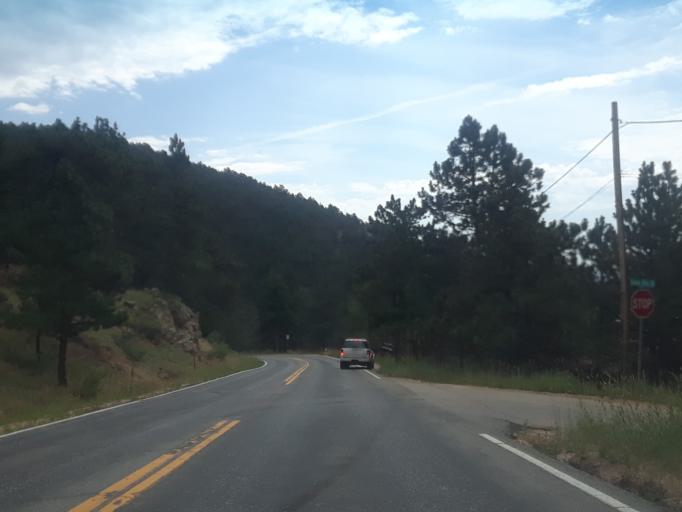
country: US
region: Colorado
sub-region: Boulder County
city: Boulder
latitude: 40.0329
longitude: -105.3190
